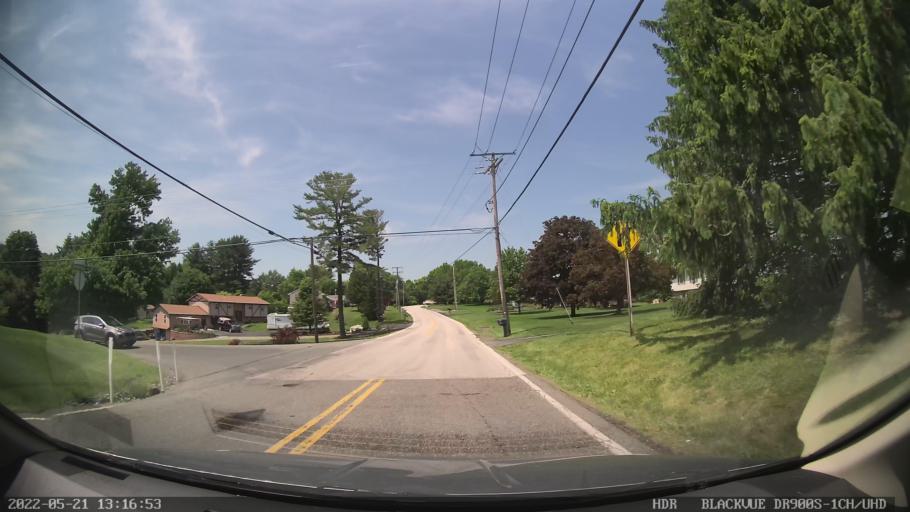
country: US
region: Pennsylvania
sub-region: Montgomery County
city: Gilbertsville
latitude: 40.3542
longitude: -75.5882
